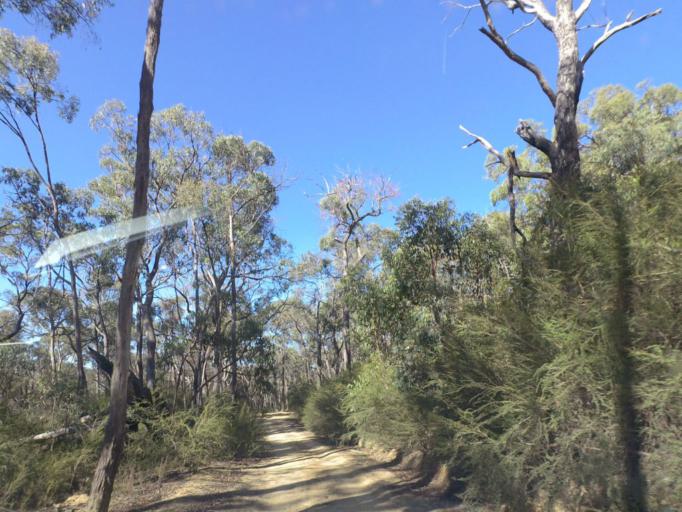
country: AU
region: Victoria
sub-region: Murrindindi
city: Kinglake West
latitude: -37.4643
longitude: 145.3692
